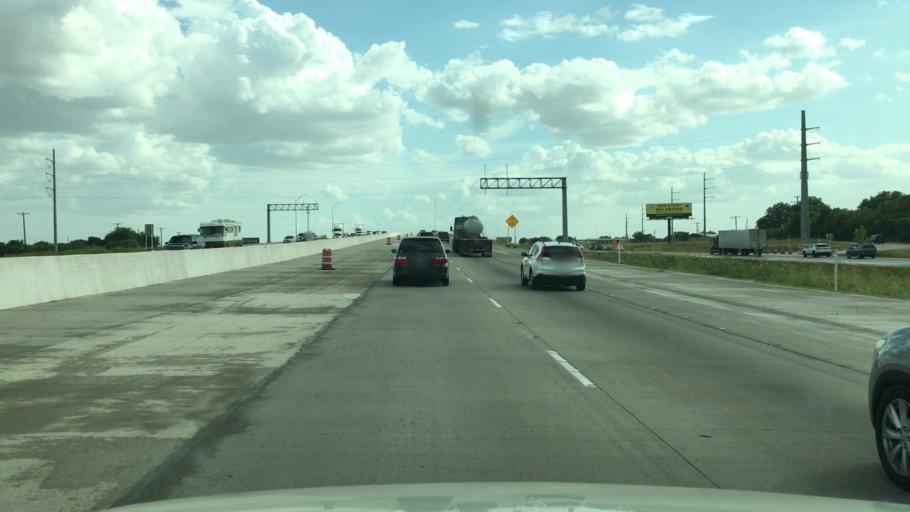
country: US
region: Texas
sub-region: McLennan County
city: Bruceville-Eddy
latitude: 31.3117
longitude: -97.2422
